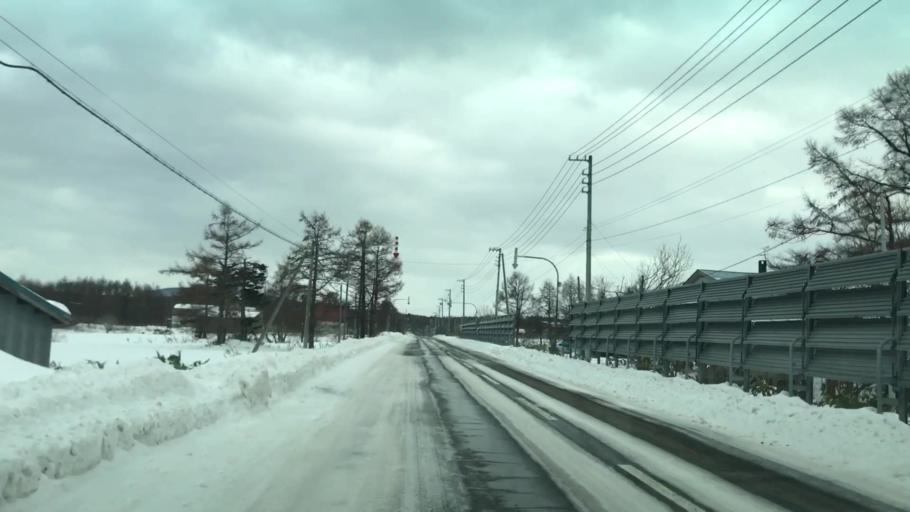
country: JP
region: Hokkaido
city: Yoichi
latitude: 43.3099
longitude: 140.5501
